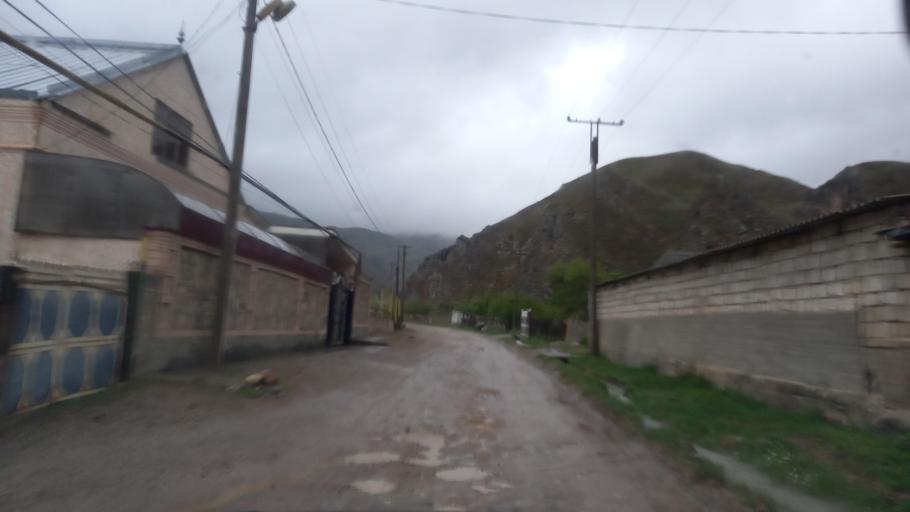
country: RU
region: Kabardino-Balkariya
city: Bylym
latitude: 43.4524
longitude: 43.0284
